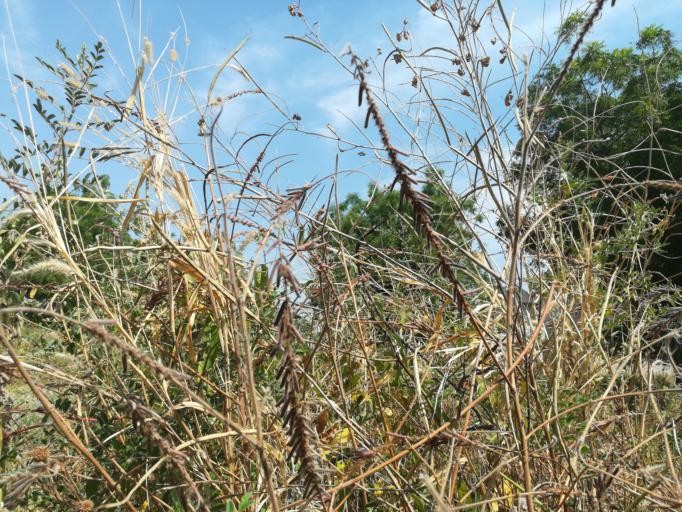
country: NG
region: Kano
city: Kano
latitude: 12.0275
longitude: 8.5206
